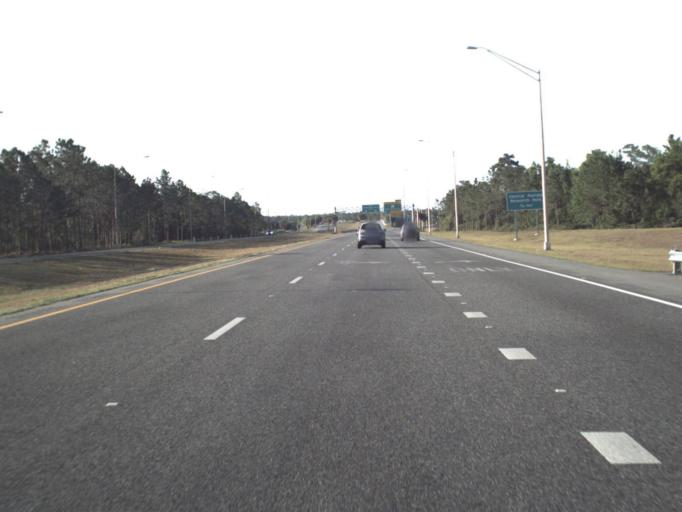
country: US
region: Florida
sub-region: Orange County
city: Alafaya
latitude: 28.5571
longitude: -81.1909
